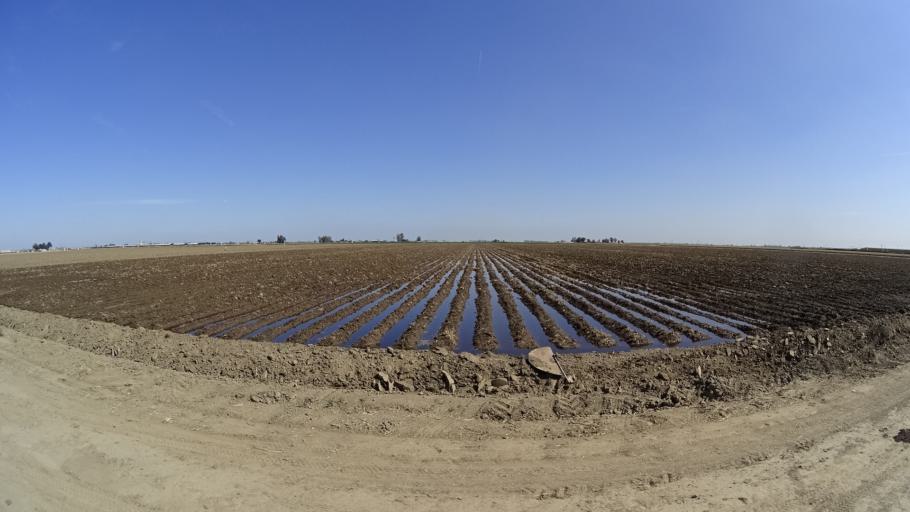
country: US
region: California
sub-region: Kings County
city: Home Garden
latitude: 36.2549
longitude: -119.6117
